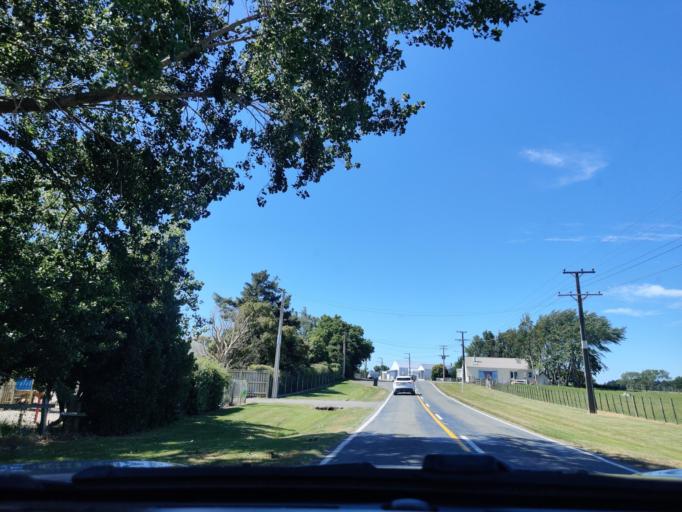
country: NZ
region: Wellington
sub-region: Upper Hutt City
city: Upper Hutt
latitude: -41.3537
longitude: 175.2046
